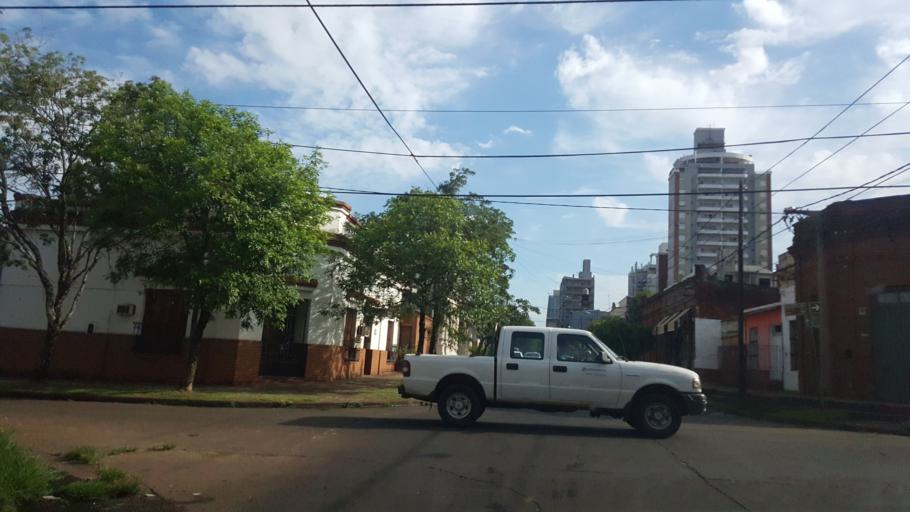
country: AR
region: Misiones
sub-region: Departamento de Capital
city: Posadas
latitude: -27.3600
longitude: -55.8926
